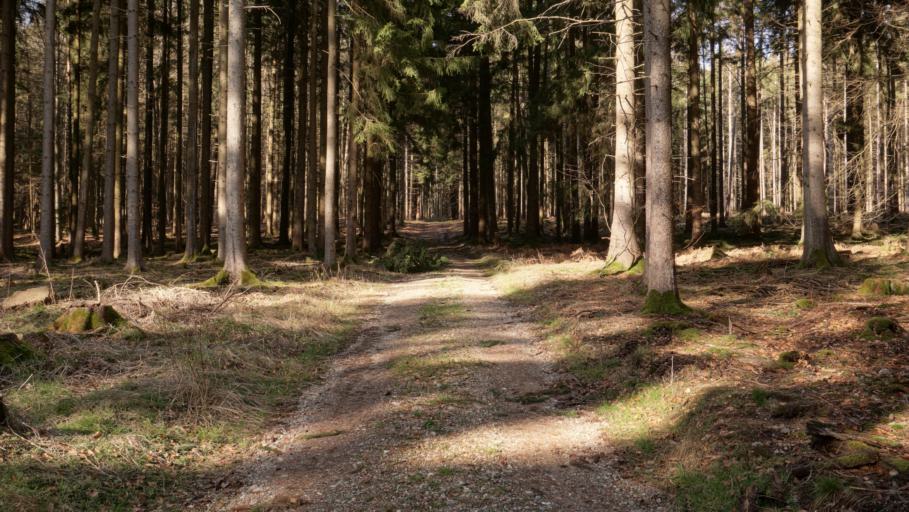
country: DE
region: Baden-Wuerttemberg
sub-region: Karlsruhe Region
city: Fahrenbach
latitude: 49.4414
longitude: 9.1214
